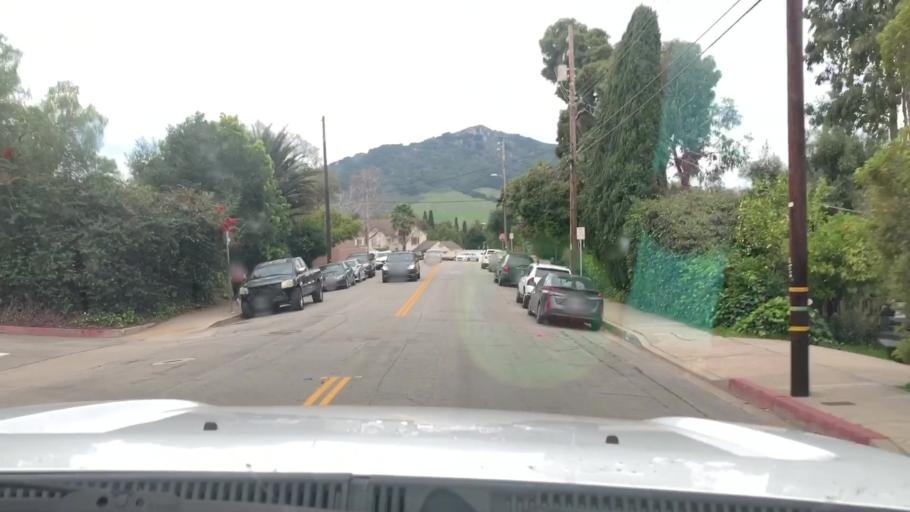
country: US
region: California
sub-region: San Luis Obispo County
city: San Luis Obispo
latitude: 35.2957
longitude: -120.6607
